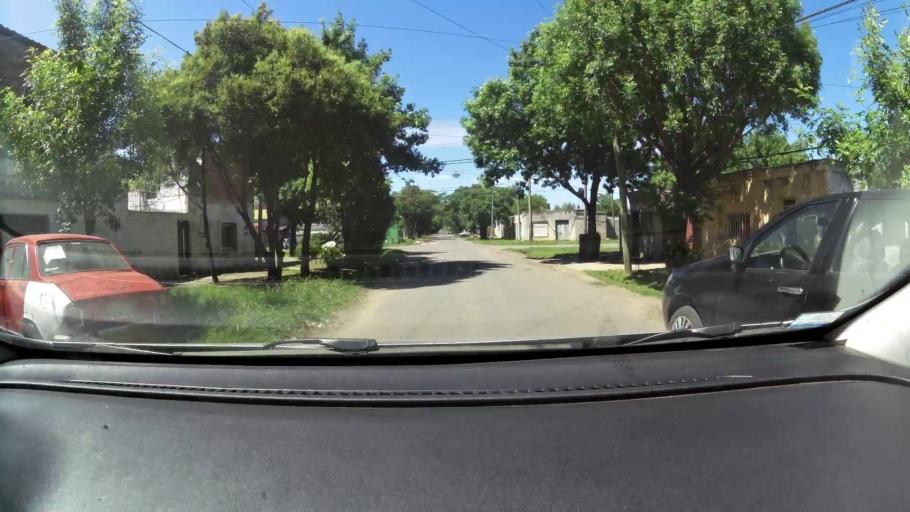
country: AR
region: Santa Fe
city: Perez
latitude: -32.9545
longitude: -60.7201
